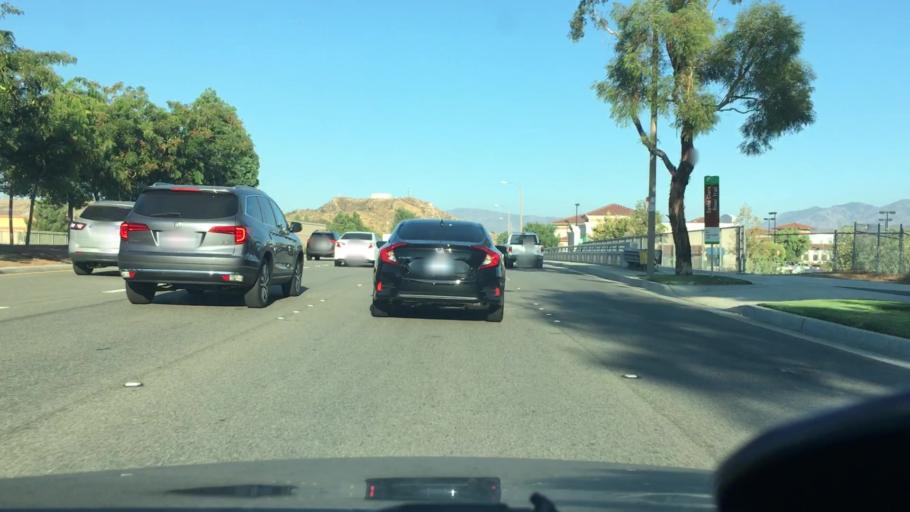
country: US
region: California
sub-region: Los Angeles County
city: Santa Clarita
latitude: 34.4282
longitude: -118.5409
